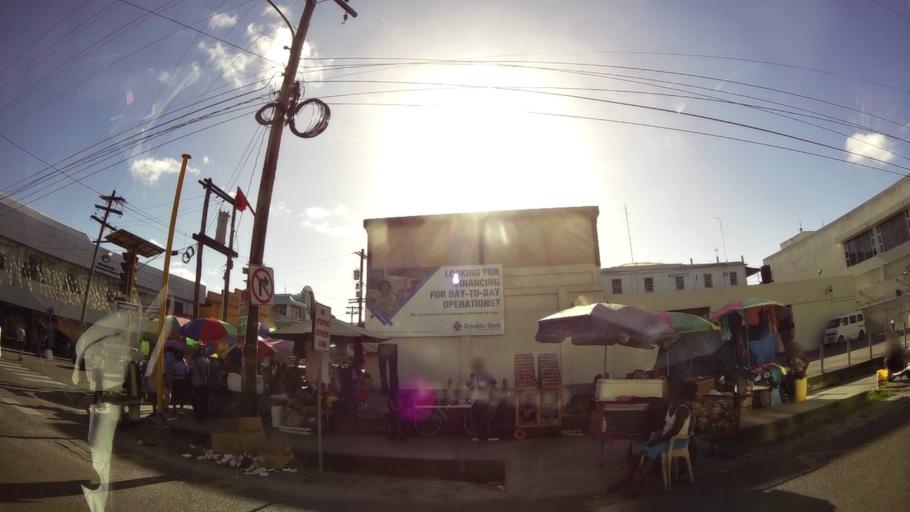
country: GY
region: Demerara-Mahaica
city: Georgetown
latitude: 6.8105
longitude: -58.1608
